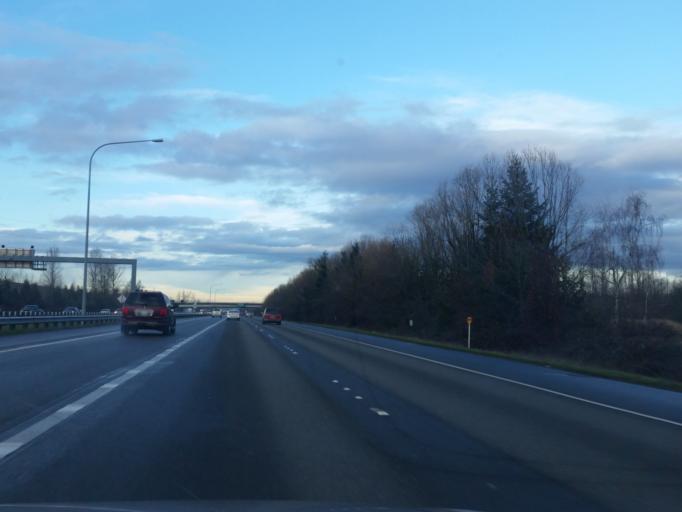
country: US
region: Washington
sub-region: King County
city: Auburn
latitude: 47.3352
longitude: -122.2447
